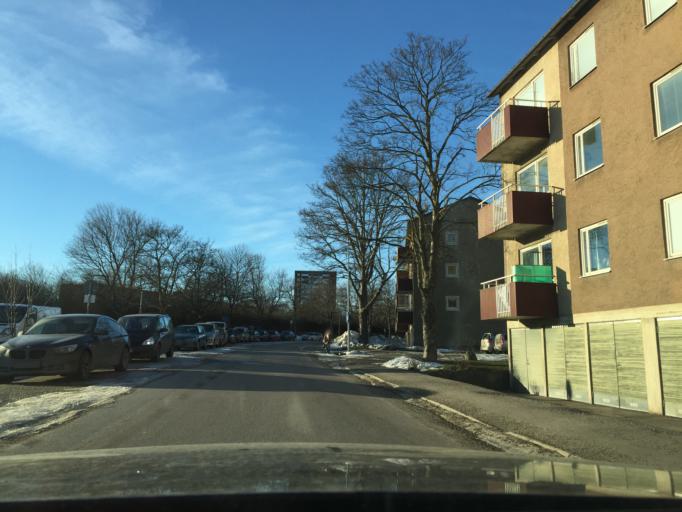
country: SE
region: Stockholm
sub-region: Stockholms Kommun
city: Bromma
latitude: 59.3597
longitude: 17.8727
